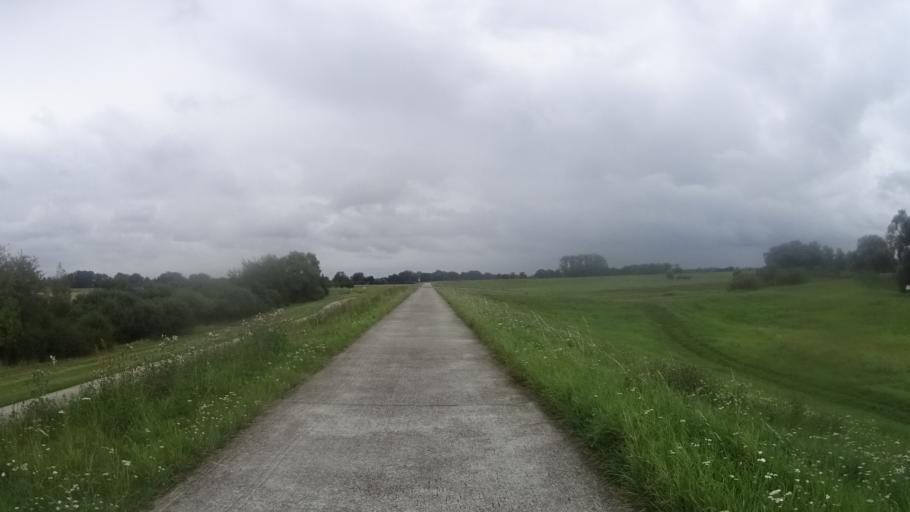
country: DE
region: Lower Saxony
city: Bleckede
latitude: 53.2974
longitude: 10.7755
